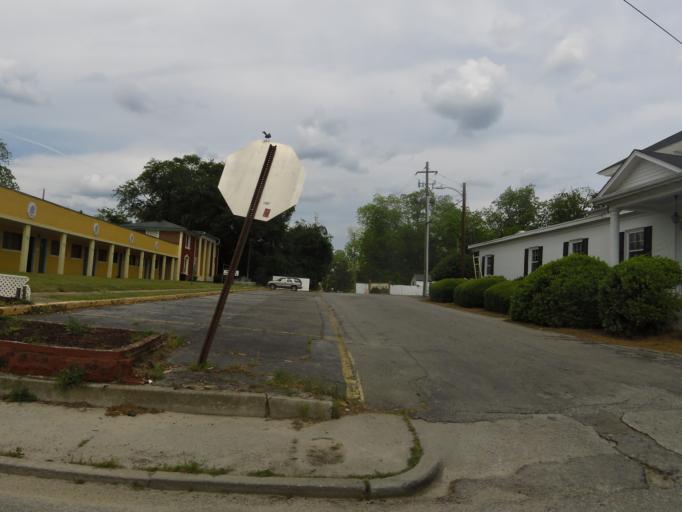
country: US
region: Georgia
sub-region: McDuffie County
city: Thomson
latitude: 33.4648
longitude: -82.5013
